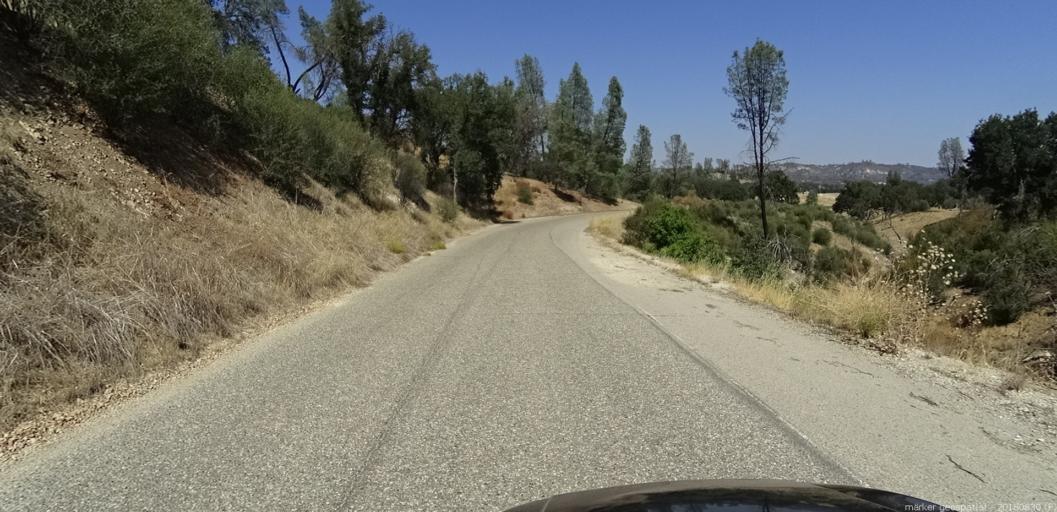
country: US
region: California
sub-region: Monterey County
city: King City
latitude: 35.9970
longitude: -121.2610
